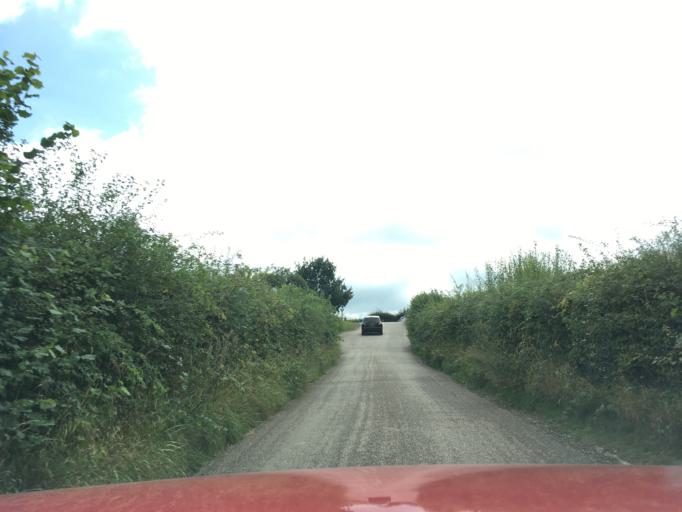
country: GB
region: England
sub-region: Kent
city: Cranbrook
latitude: 51.1109
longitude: 0.5723
